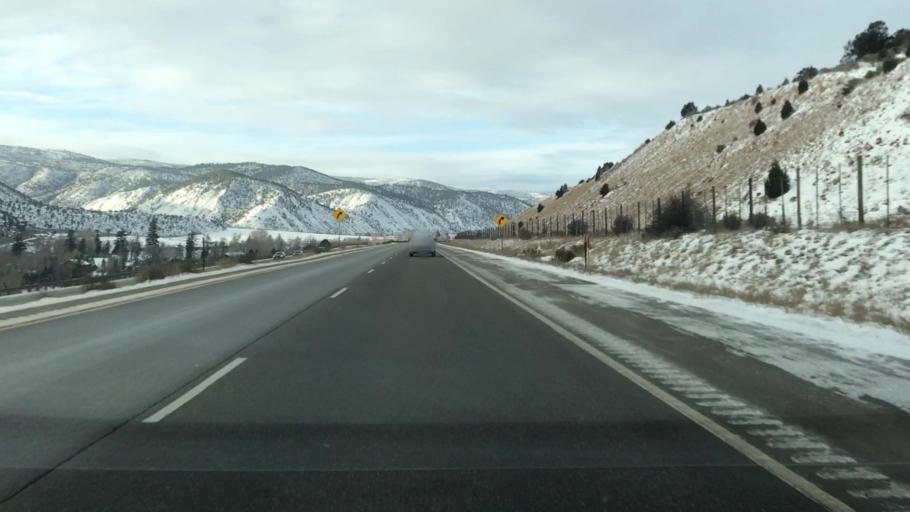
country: US
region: Colorado
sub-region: Eagle County
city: Eagle
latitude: 39.6880
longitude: -106.7520
